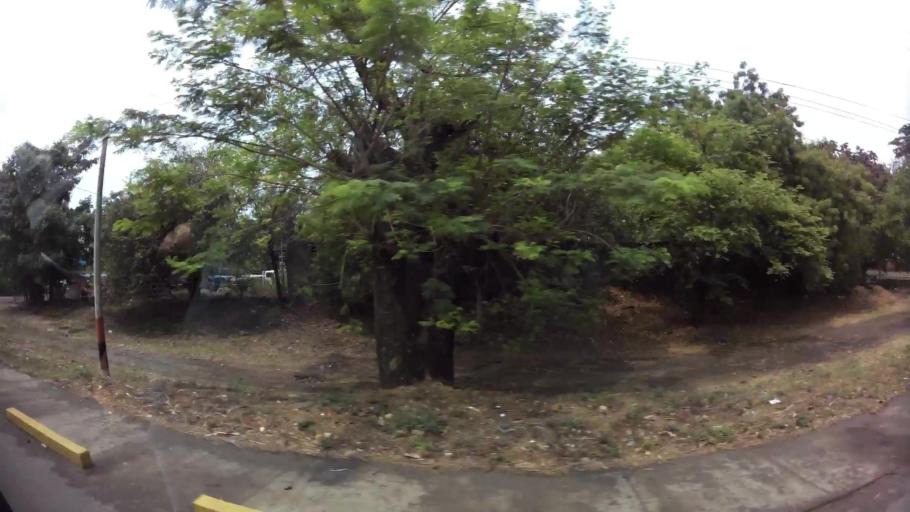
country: NI
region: Chinandega
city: Chinandega
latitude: 12.6395
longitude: -87.1276
